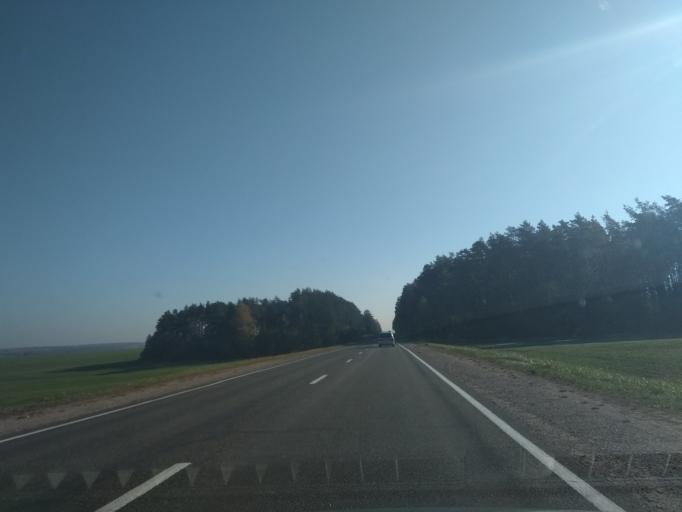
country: BY
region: Grodnenskaya
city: Zel'va
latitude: 53.1332
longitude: 24.9966
